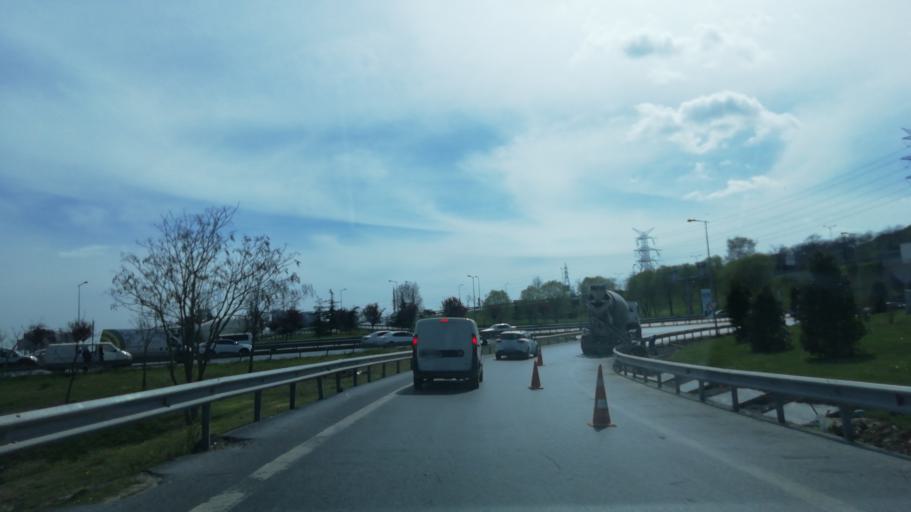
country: TR
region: Istanbul
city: Esenler
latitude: 41.0572
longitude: 28.8875
